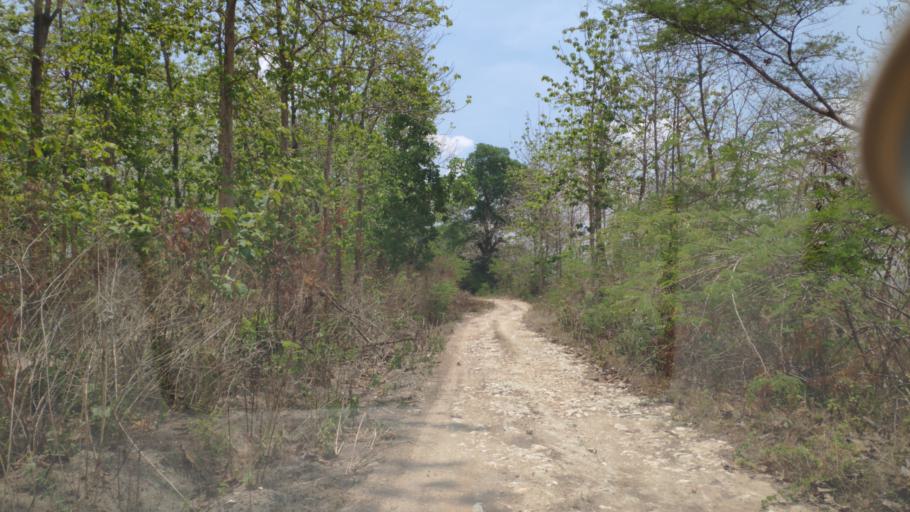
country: ID
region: Central Java
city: Botoh
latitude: -7.0738
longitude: 111.4784
